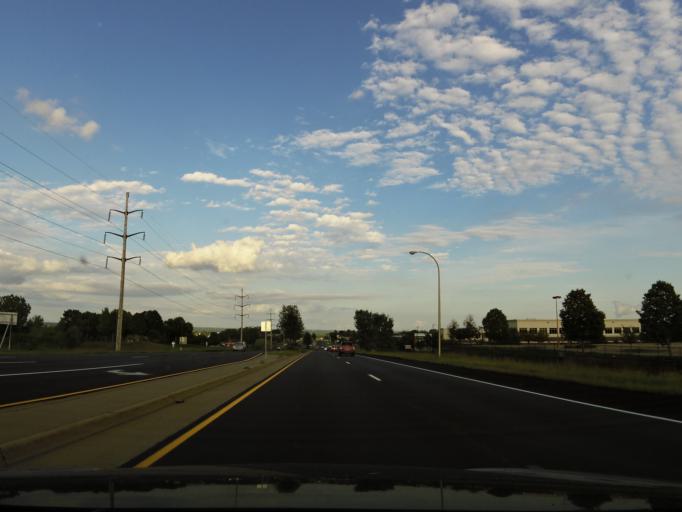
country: US
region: Minnesota
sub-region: Dakota County
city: Hastings
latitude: 44.7384
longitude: -92.8888
